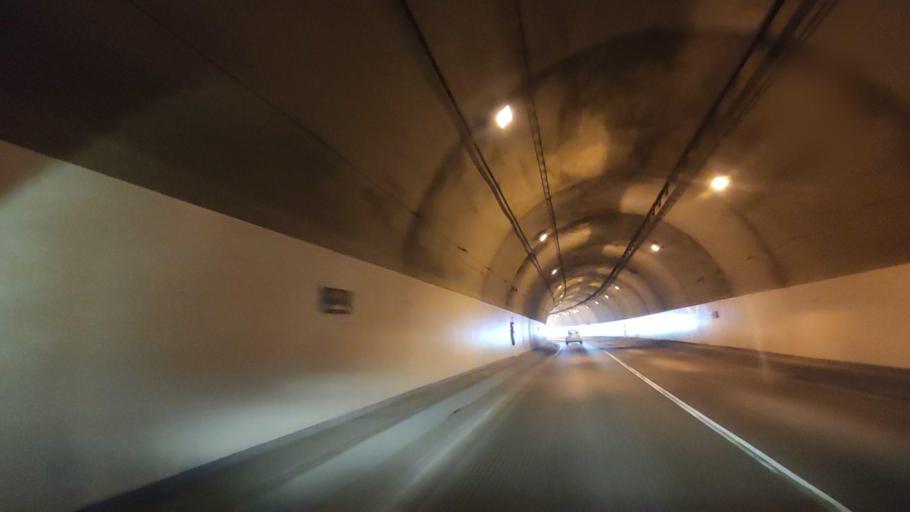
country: JP
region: Hokkaido
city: Ishikari
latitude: 43.4524
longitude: 141.4094
